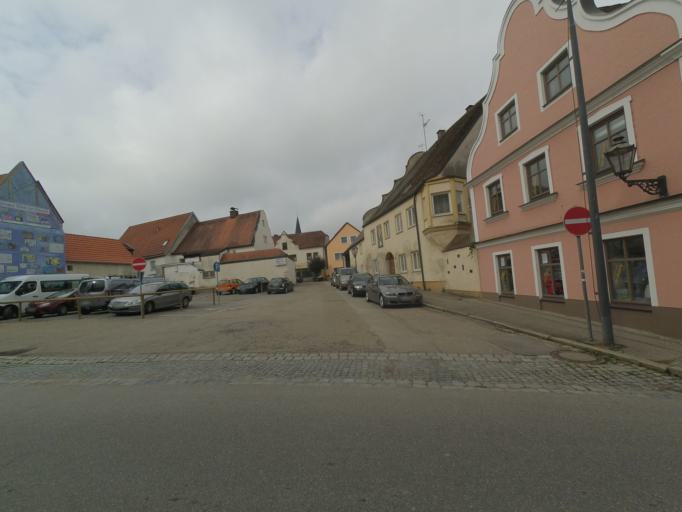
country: DE
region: Bavaria
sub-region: Lower Bavaria
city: Geiselhoring
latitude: 48.8263
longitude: 12.3923
